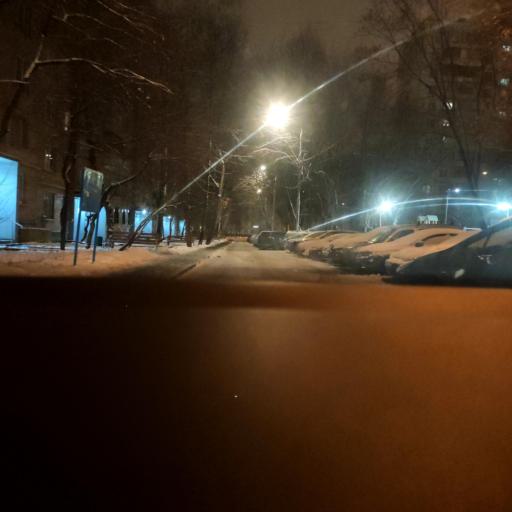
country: RU
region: Moscow
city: Strogino
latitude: 55.8482
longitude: 37.4276
